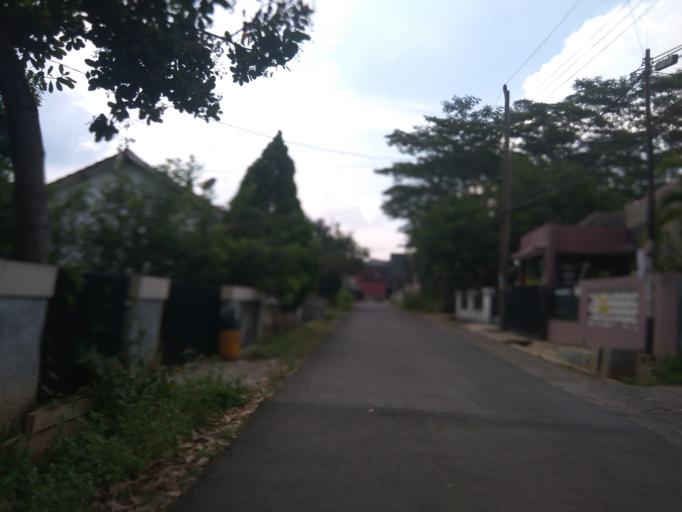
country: ID
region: Central Java
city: Semarang
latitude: -7.0649
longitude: 110.4472
